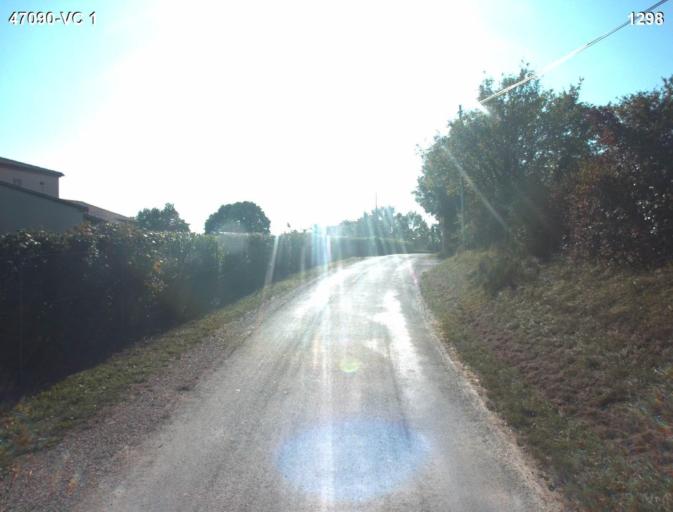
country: FR
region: Aquitaine
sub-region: Departement du Lot-et-Garonne
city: Nerac
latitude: 44.1639
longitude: 0.3841
